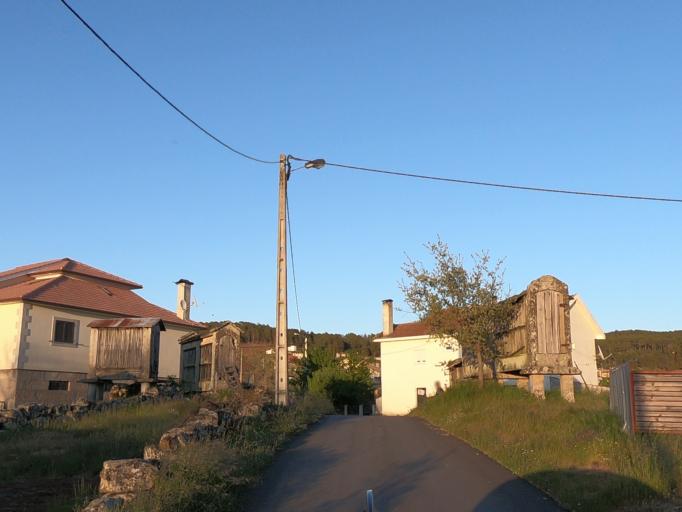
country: PT
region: Vila Real
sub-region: Vila Real
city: Vila Real
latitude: 41.3363
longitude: -7.6671
